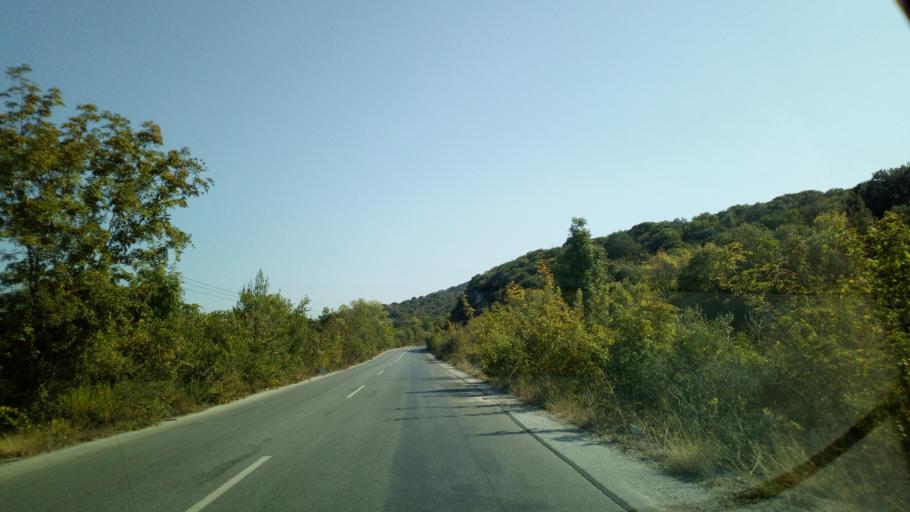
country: GR
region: Central Macedonia
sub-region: Nomos Thessalonikis
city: Stavros
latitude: 40.6274
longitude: 23.7664
